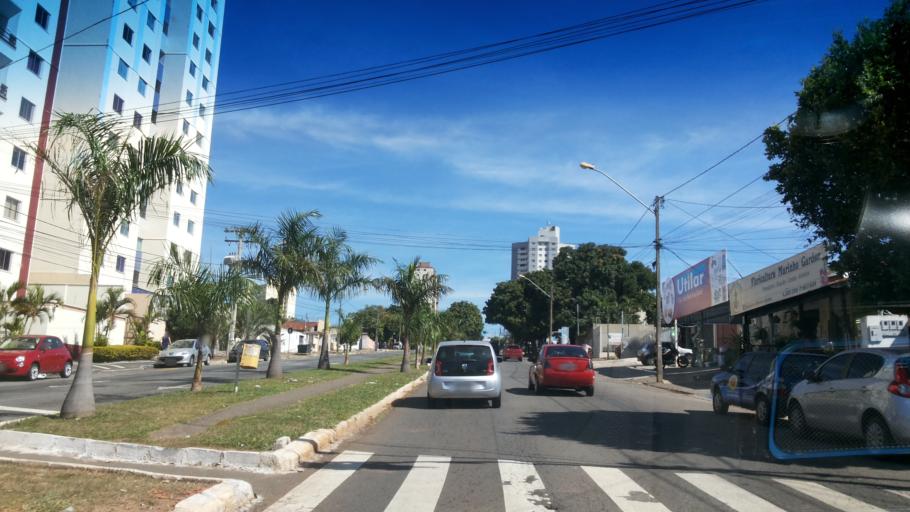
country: BR
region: Goias
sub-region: Goiania
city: Goiania
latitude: -16.7127
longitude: -49.2470
